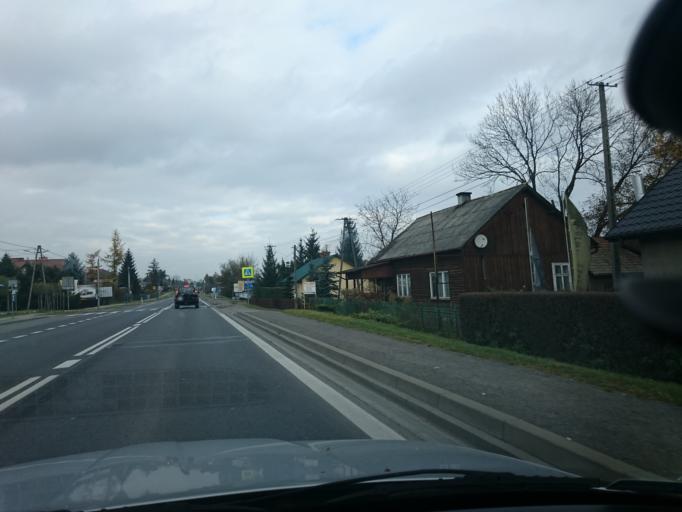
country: PL
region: Lesser Poland Voivodeship
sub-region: Powiat krakowski
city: Michalowice
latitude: 50.1618
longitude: 19.9796
